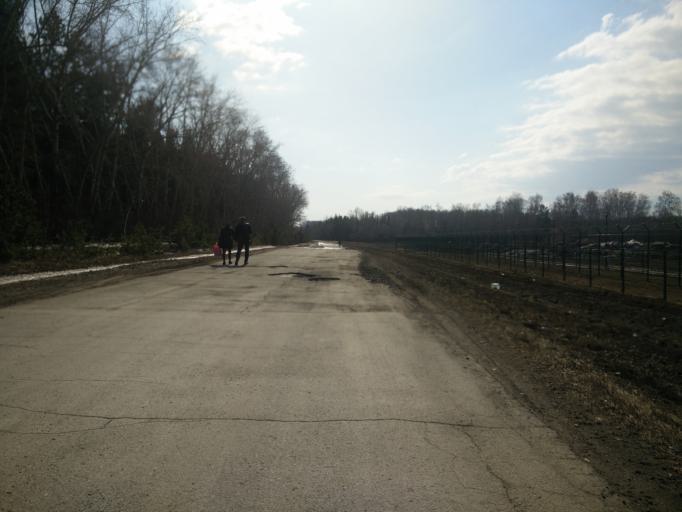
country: RU
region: Novosibirsk
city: Berdsk
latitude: 54.7621
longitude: 83.0738
